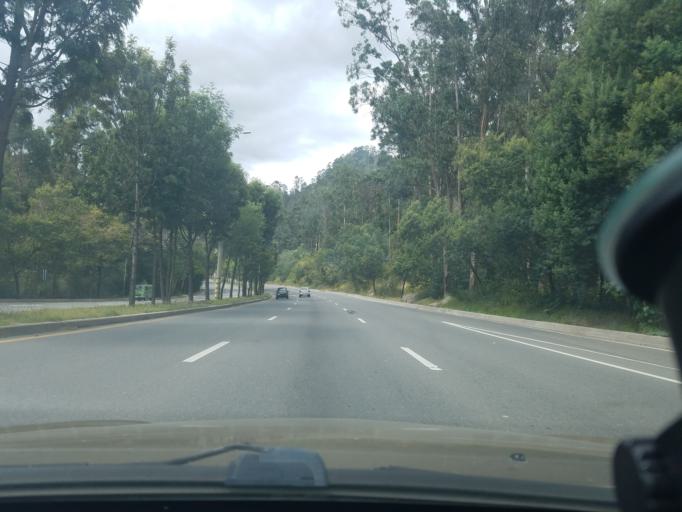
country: EC
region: Azuay
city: Llacao
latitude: -2.8773
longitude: -78.9418
